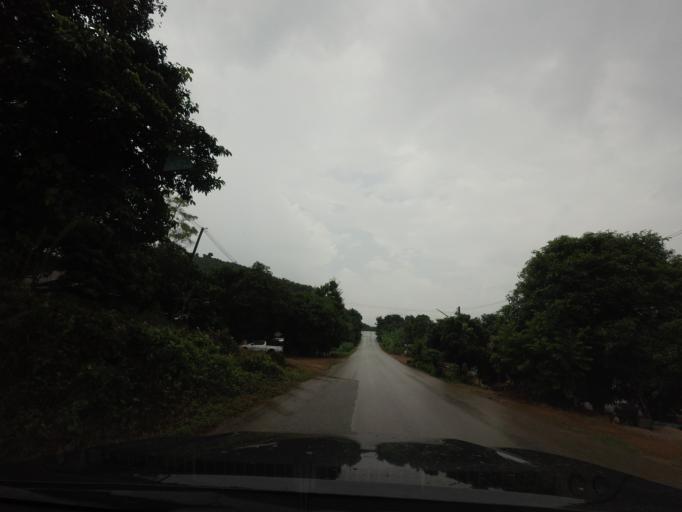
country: TH
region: Loei
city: Pak Chom
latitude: 18.1092
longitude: 101.9777
